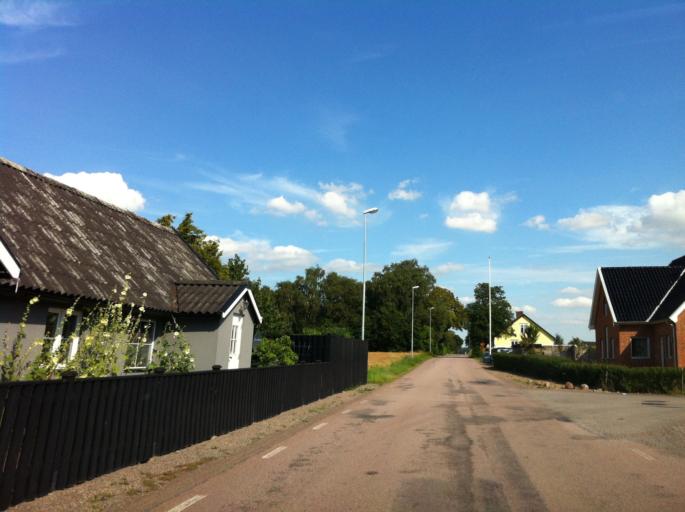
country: SE
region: Skane
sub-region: Helsingborg
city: Barslov
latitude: 55.9989
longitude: 12.8189
